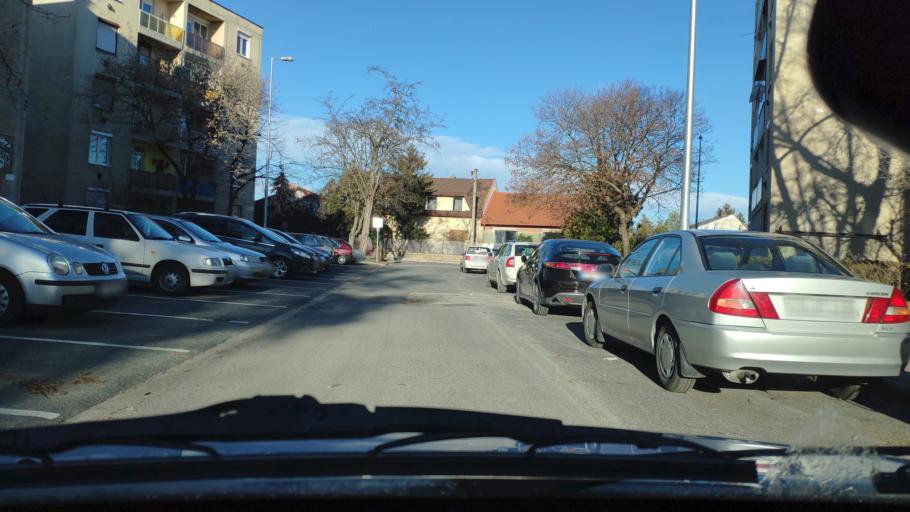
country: HU
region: Budapest
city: Budapest XXI. keruelet
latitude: 47.4085
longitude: 19.0776
